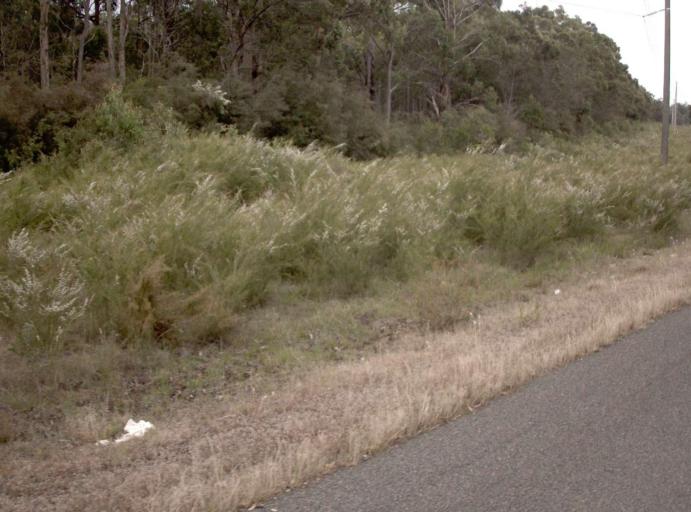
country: AU
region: Victoria
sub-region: East Gippsland
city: Lakes Entrance
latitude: -37.7249
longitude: 147.9532
